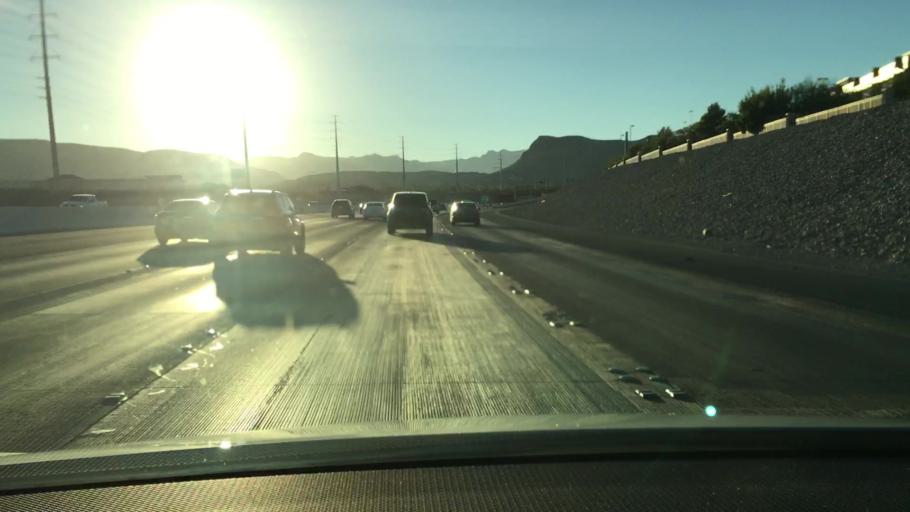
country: US
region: Nevada
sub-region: Clark County
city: Summerlin South
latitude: 36.1197
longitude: -115.3198
